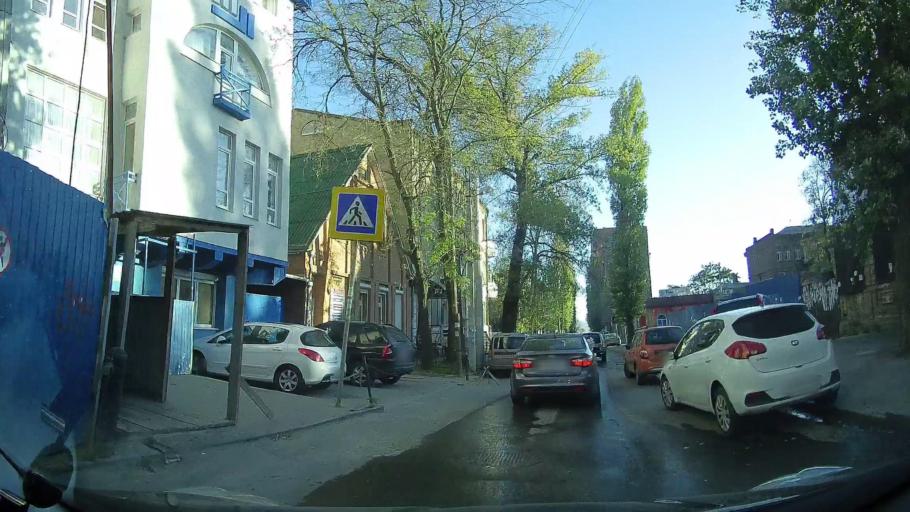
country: RU
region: Rostov
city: Rostov-na-Donu
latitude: 47.2256
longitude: 39.7367
